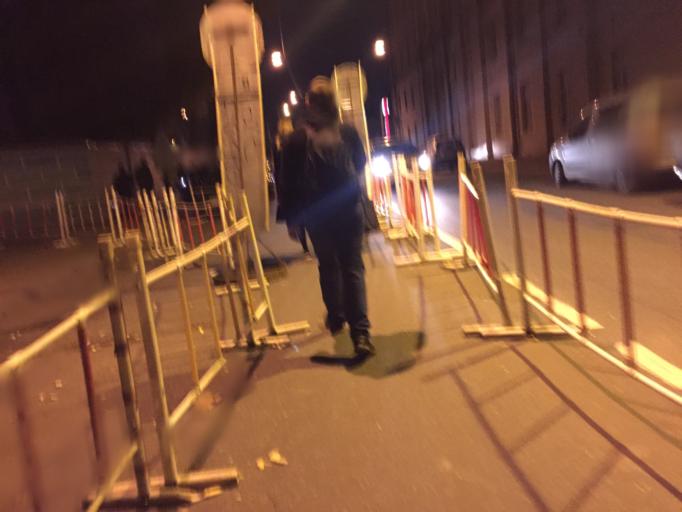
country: RU
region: St.-Petersburg
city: Vasyl'evsky Ostrov
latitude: 59.9256
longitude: 30.2407
